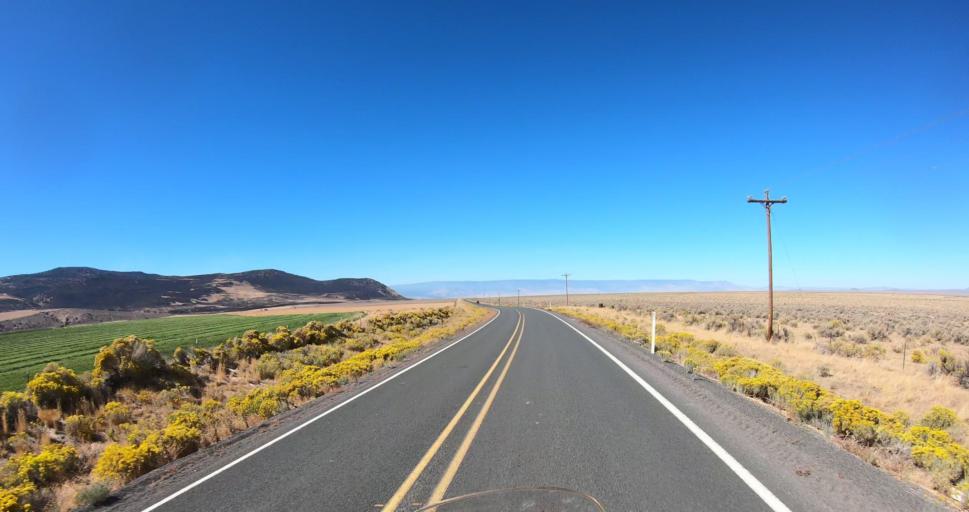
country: US
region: Oregon
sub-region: Lake County
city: Lakeview
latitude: 42.7058
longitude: -120.5511
